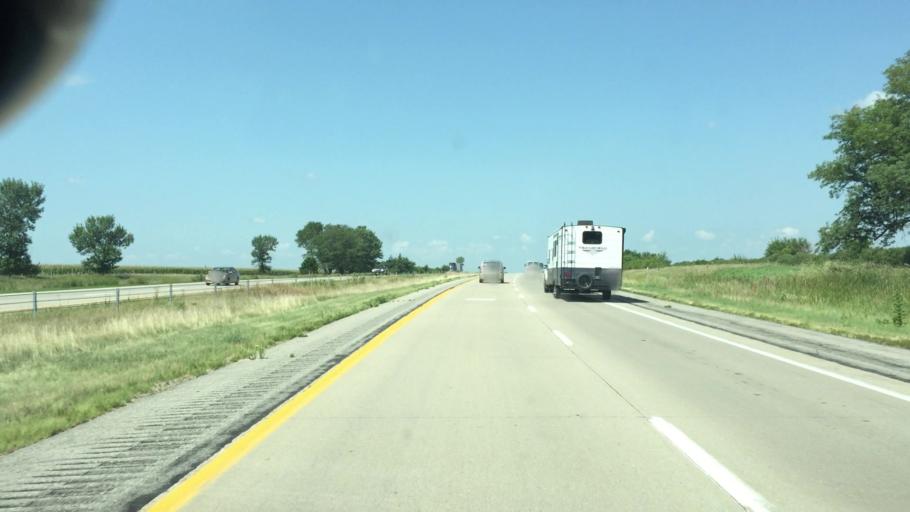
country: US
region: Iowa
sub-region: Jasper County
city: Newton
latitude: 41.6800
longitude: -92.9422
